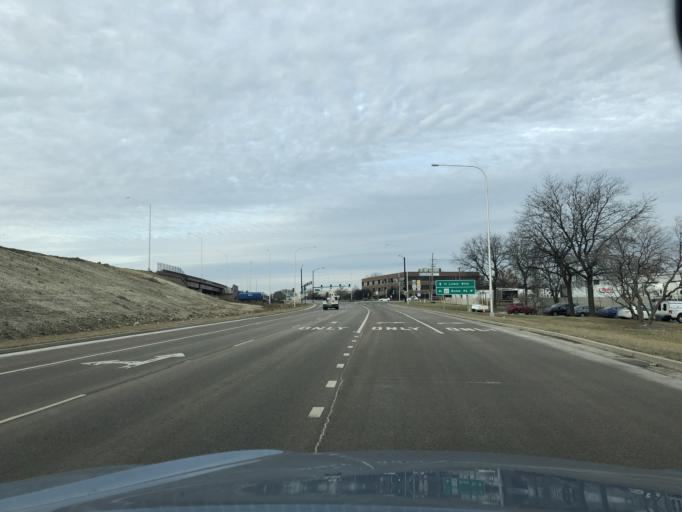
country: US
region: Illinois
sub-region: Cook County
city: Elk Grove Village
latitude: 41.9832
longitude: -87.9571
